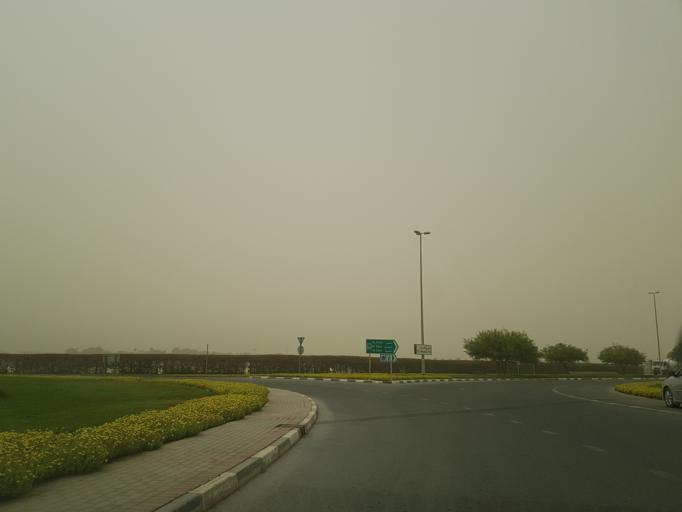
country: AE
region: Dubai
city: Dubai
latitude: 25.1523
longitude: 55.2923
